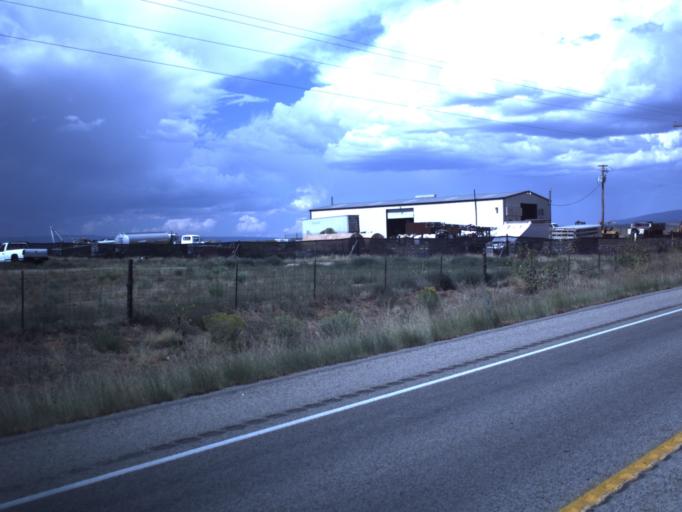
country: US
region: Utah
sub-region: San Juan County
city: Blanding
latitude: 37.5831
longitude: -109.4782
